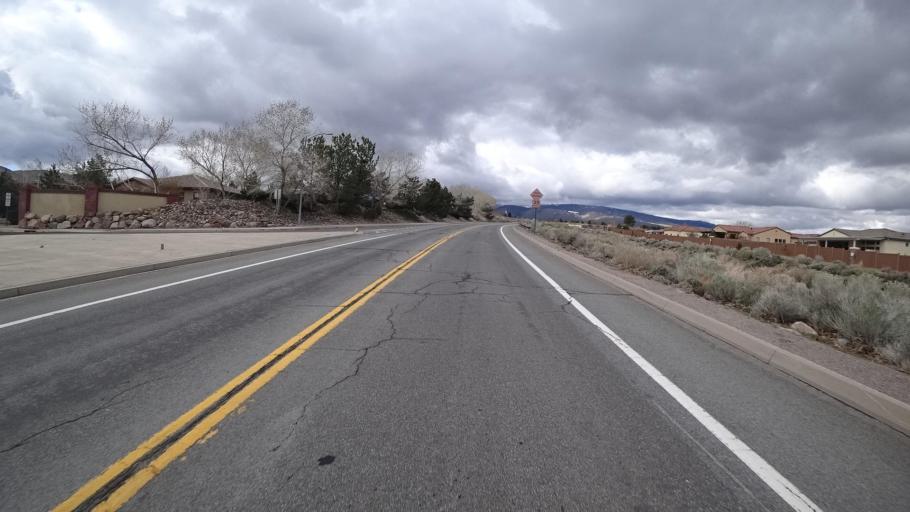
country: US
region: Nevada
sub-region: Washoe County
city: Sparks
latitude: 39.4044
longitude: -119.7682
